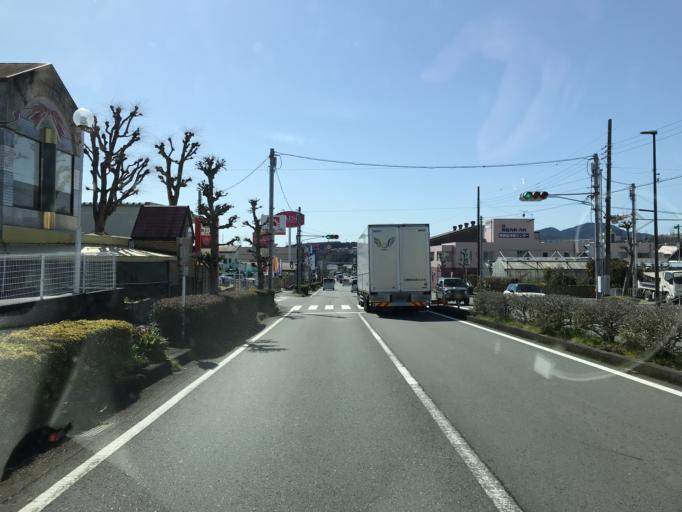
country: JP
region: Shizuoka
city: Fujinomiya
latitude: 35.2187
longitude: 138.6284
